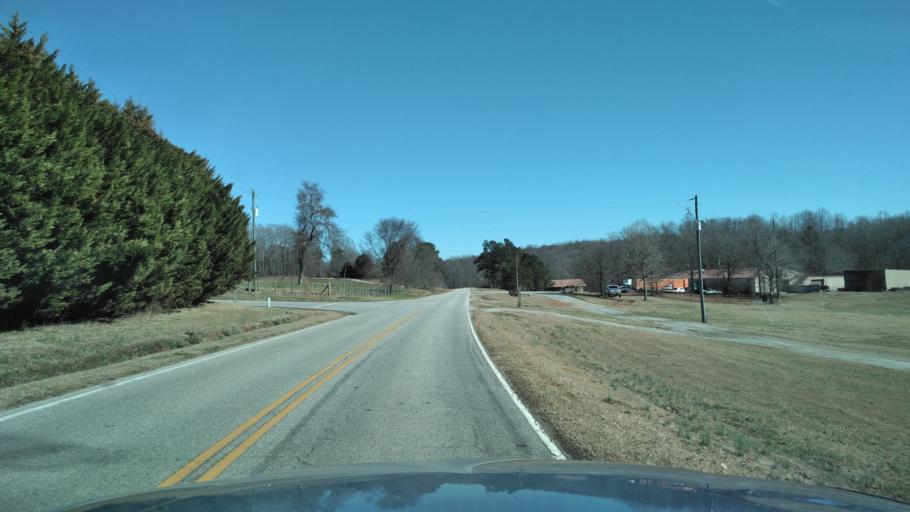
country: US
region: Georgia
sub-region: Hall County
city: Lula
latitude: 34.3189
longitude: -83.6958
